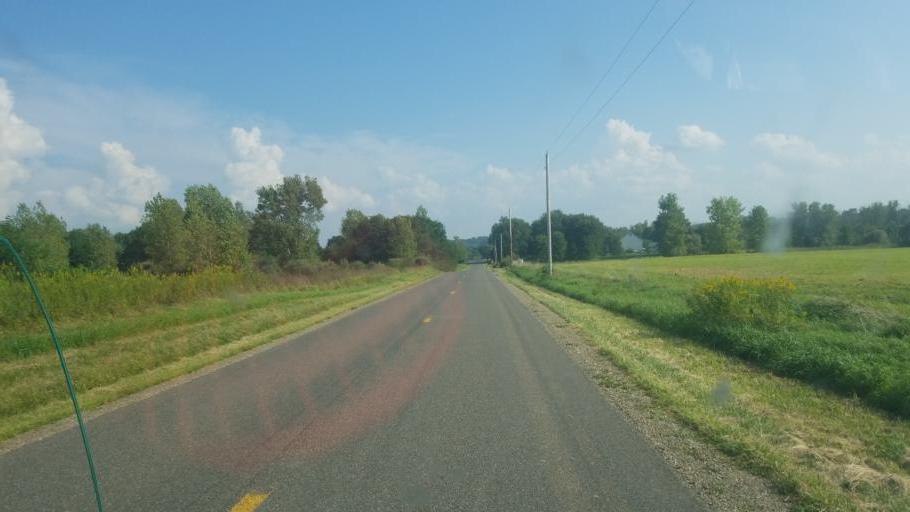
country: US
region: Ohio
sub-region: Medina County
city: Westfield Center
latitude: 41.0019
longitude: -81.9608
